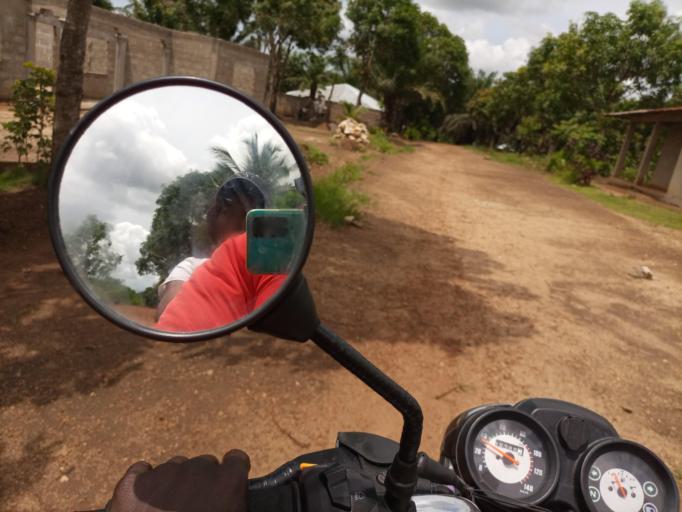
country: SL
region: Southern Province
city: Baoma
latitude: 7.9737
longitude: -11.7116
